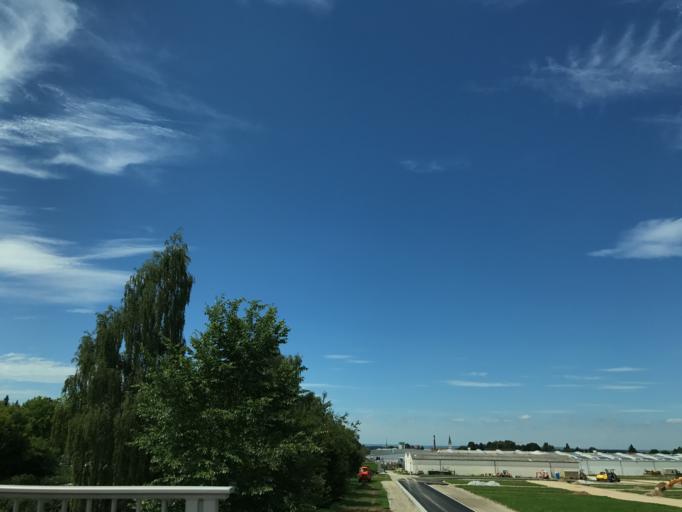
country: DE
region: Baden-Wuerttemberg
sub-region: Tuebingen Region
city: Saulgau
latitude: 48.0056
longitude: 9.5109
